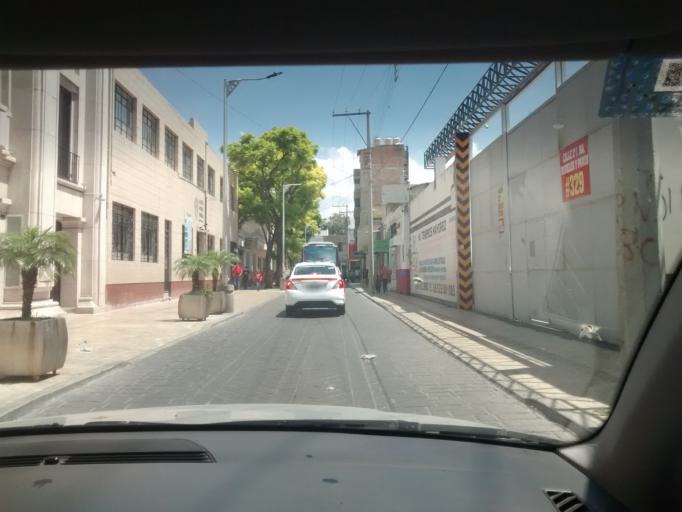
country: MX
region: Puebla
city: Tehuacan
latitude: 18.4599
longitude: -97.3926
